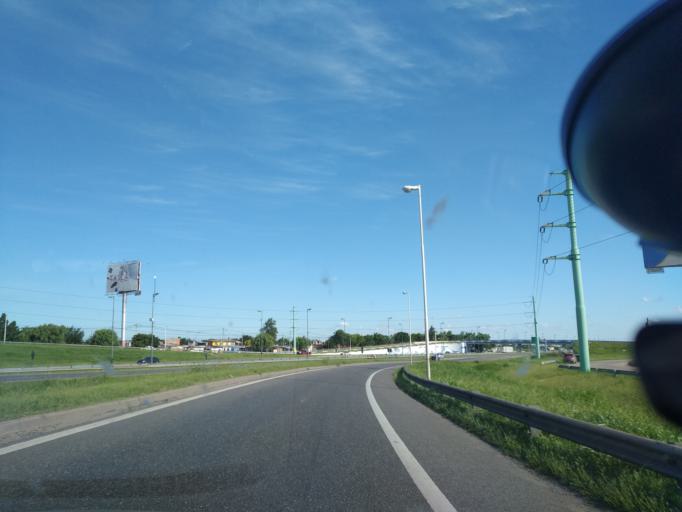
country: AR
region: Santa Fe
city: Gobernador Galvez
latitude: -33.0163
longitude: -60.6651
